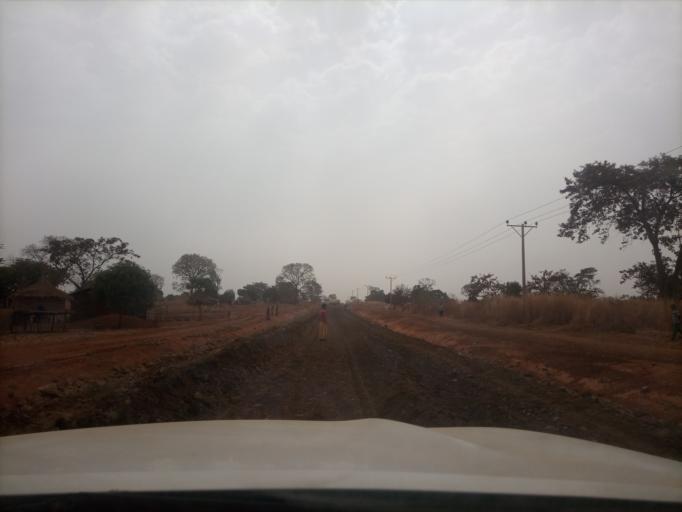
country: ET
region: Oromiya
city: Mendi
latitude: 10.1283
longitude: 35.1312
